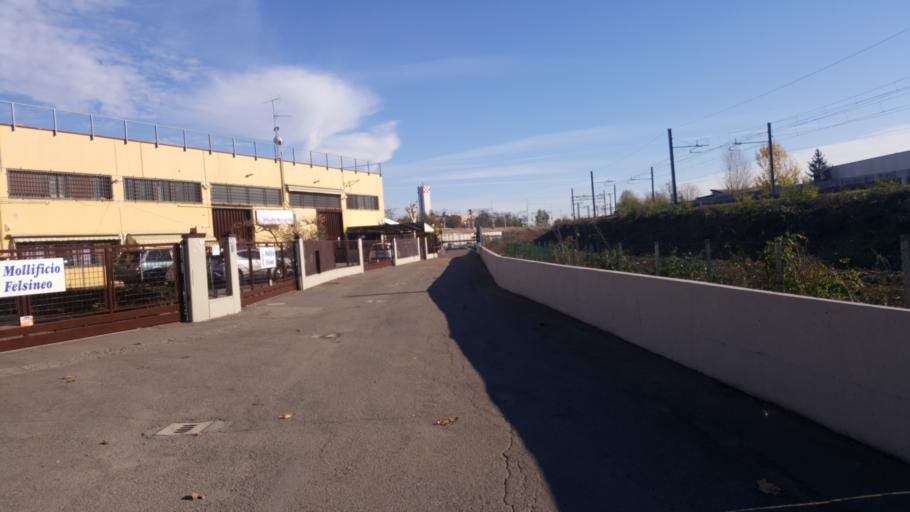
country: IT
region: Emilia-Romagna
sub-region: Provincia di Bologna
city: Calderara di Reno
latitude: 44.5468
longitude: 11.2837
